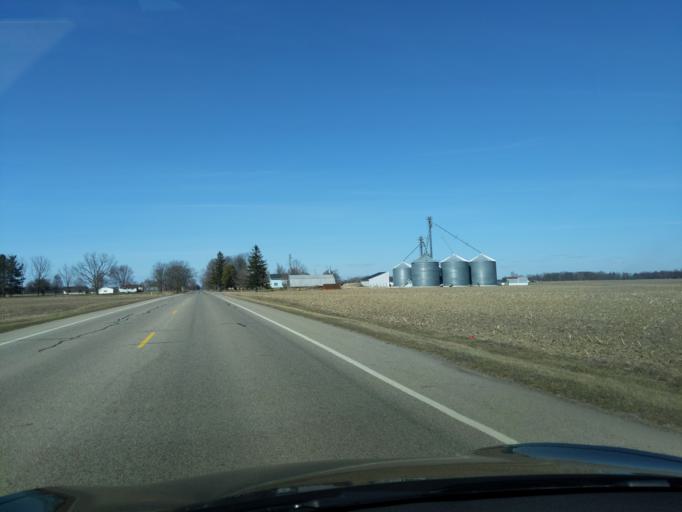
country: US
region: Michigan
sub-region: Ionia County
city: Lake Odessa
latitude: 42.8046
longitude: -85.1335
